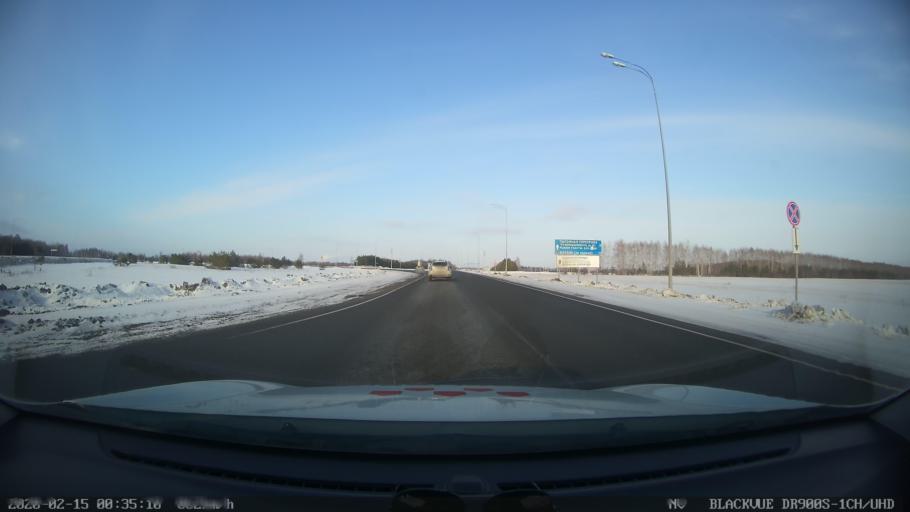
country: RU
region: Tatarstan
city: Verkhniy Uslon
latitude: 55.7060
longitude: 48.8915
